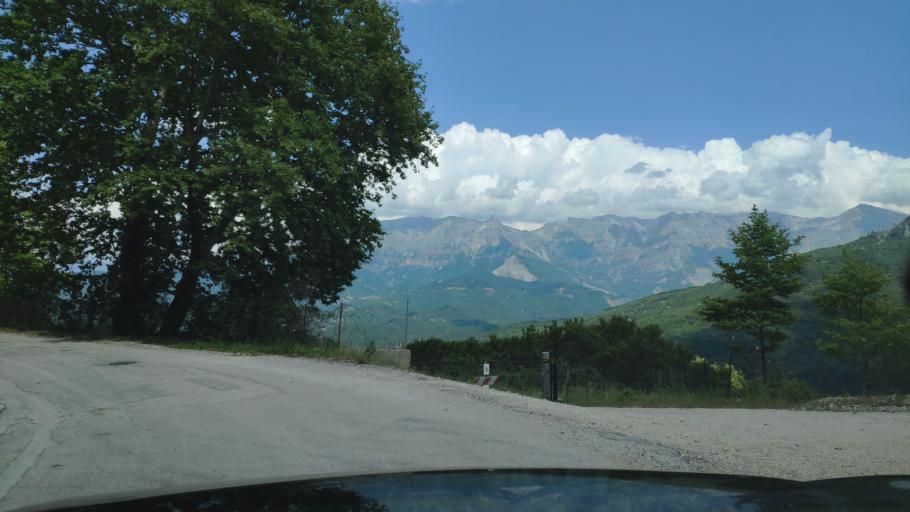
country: GR
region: Epirus
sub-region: Nomos Artas
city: Agios Dimitrios
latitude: 39.4381
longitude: 21.0141
